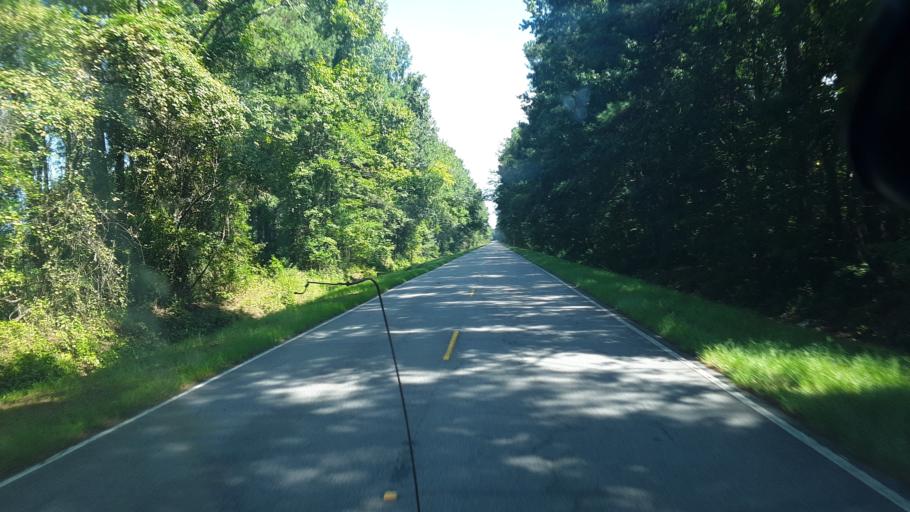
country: US
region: South Carolina
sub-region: Hampton County
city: Hampton
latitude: 33.0023
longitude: -81.0480
